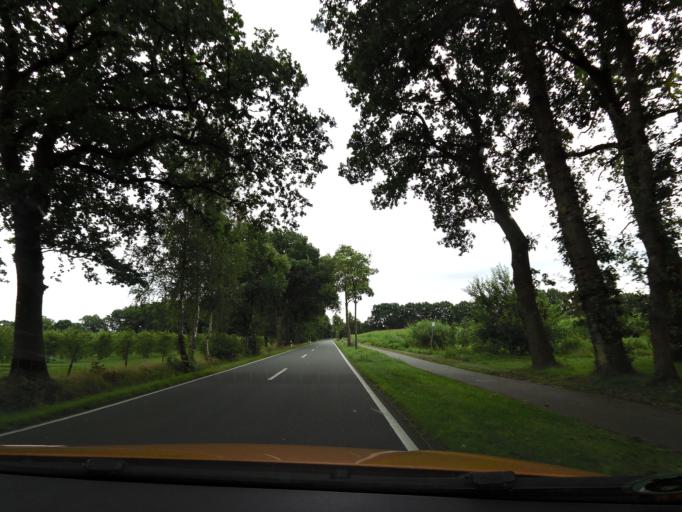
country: DE
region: Lower Saxony
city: Wiefelstede
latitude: 53.1943
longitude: 8.1381
